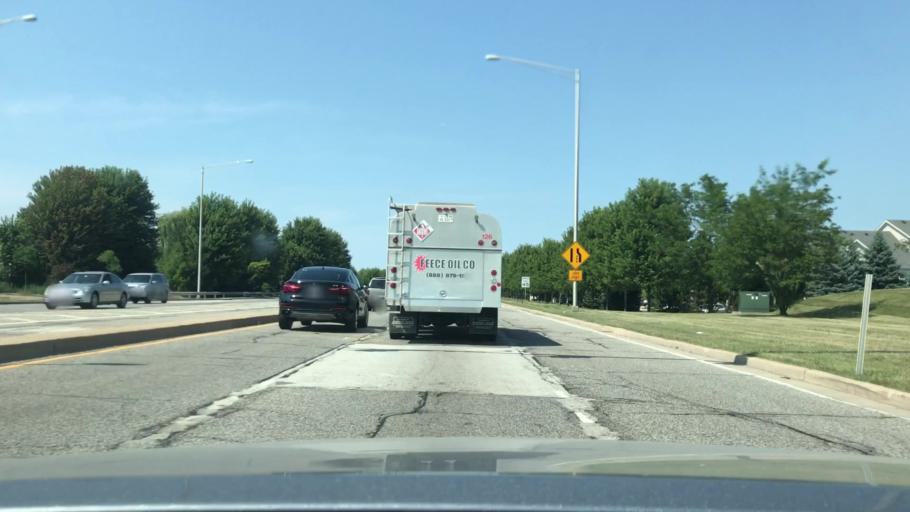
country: US
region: Illinois
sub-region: Kane County
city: Batavia
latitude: 41.8175
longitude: -88.2796
